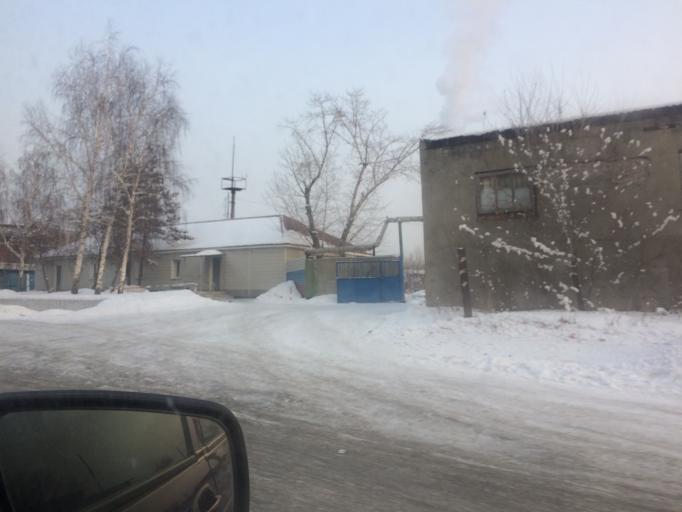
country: RU
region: Chelyabinsk
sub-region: Gorod Magnitogorsk
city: Magnitogorsk
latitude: 53.4654
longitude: 59.0717
